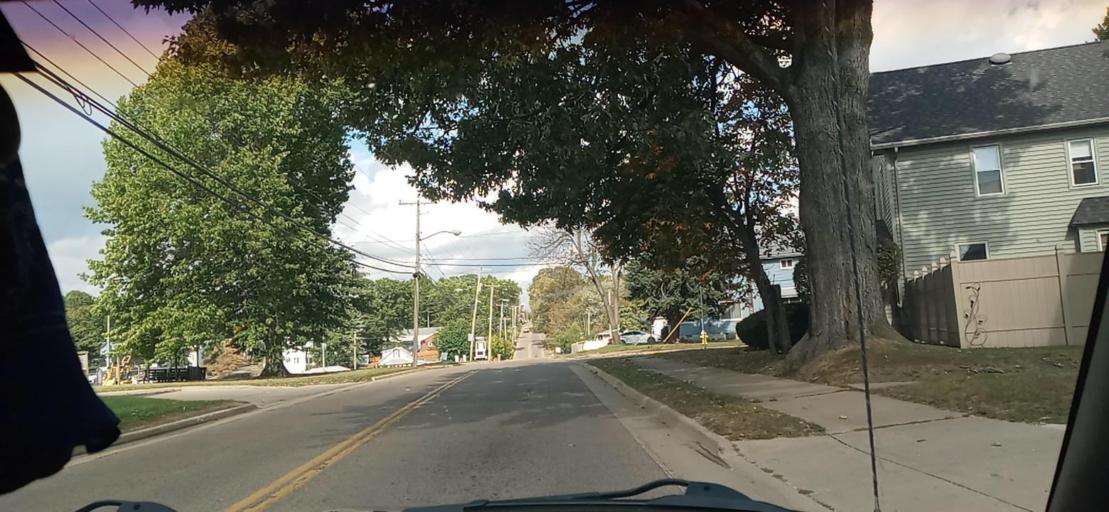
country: US
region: Ohio
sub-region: Summit County
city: Akron
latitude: 41.0922
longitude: -81.4963
